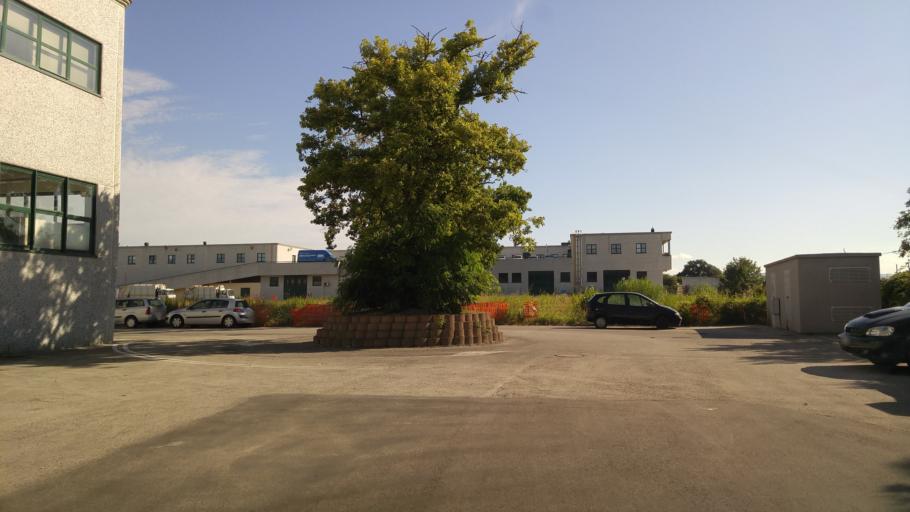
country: IT
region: The Marches
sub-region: Provincia di Pesaro e Urbino
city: Rosciano
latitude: 43.8155
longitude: 13.0036
